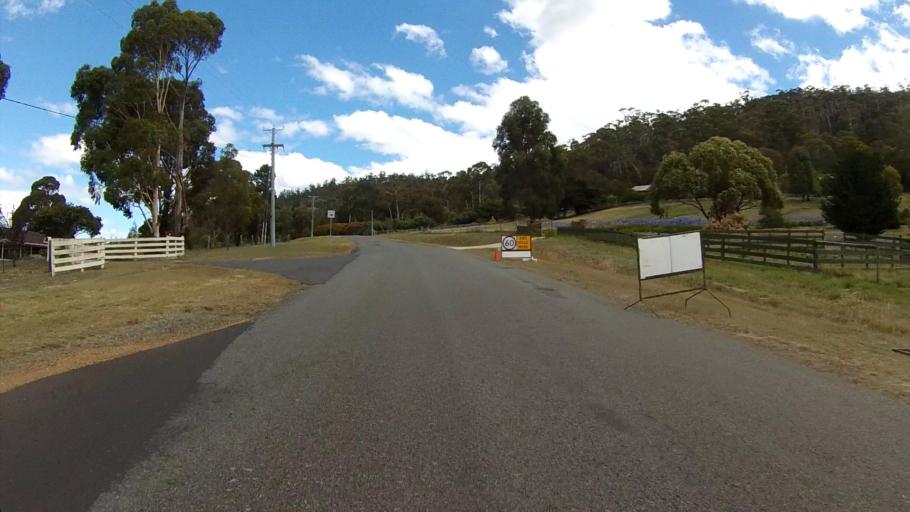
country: AU
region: Tasmania
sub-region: Clarence
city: Acton Park
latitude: -42.8621
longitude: 147.4705
